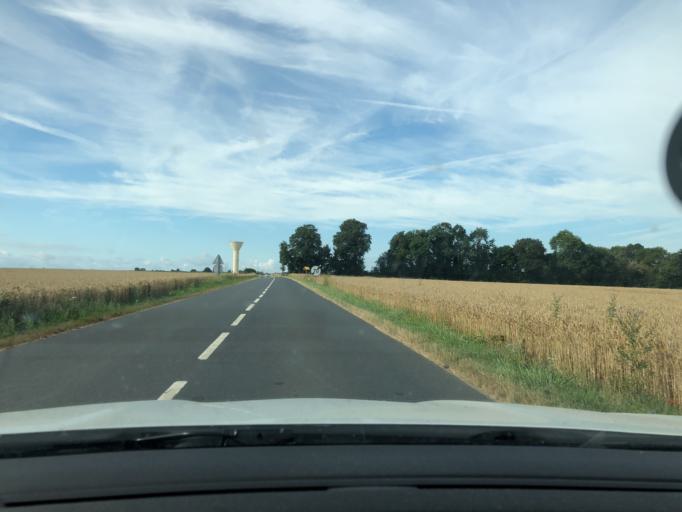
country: FR
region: Lower Normandy
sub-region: Departement du Calvados
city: Saint-Vigor-le-Grand
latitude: 49.2630
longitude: -0.6210
